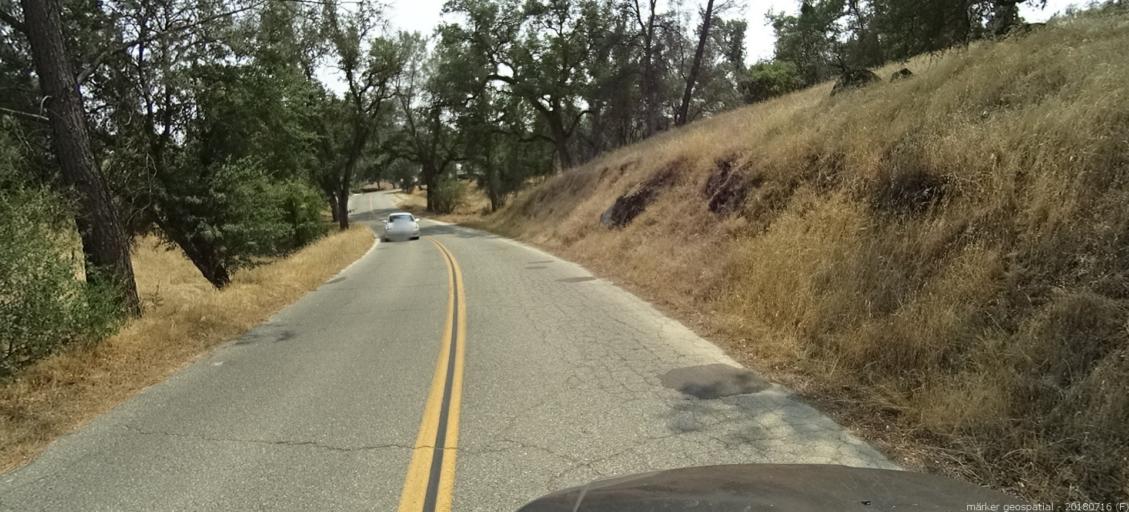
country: US
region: California
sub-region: Madera County
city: Yosemite Lakes
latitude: 37.2261
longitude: -119.7776
